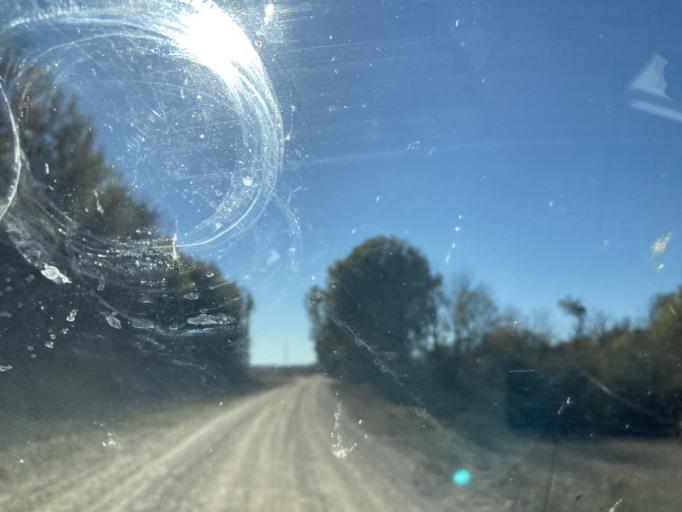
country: US
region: Mississippi
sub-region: Sharkey County
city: Rolling Fork
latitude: 32.7568
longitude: -90.6892
